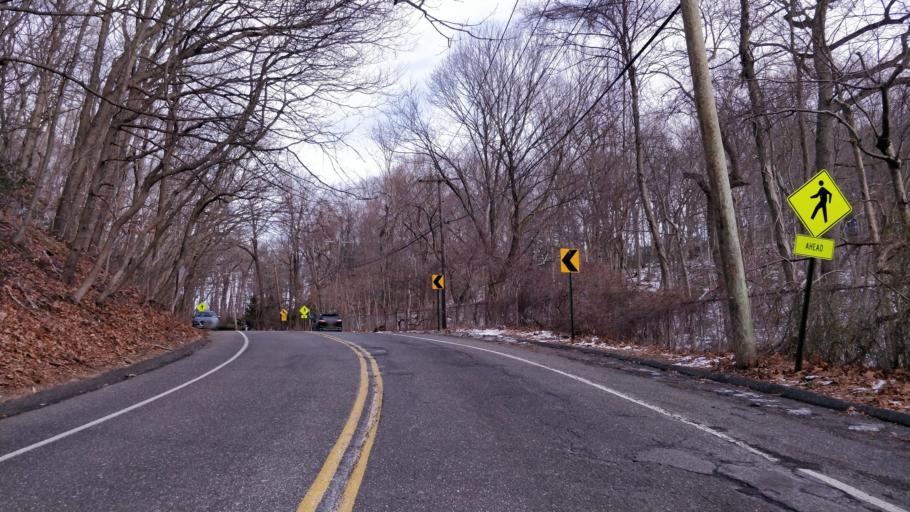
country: US
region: New York
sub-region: Nassau County
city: Laurel Hollow
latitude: 40.8581
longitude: -73.4593
